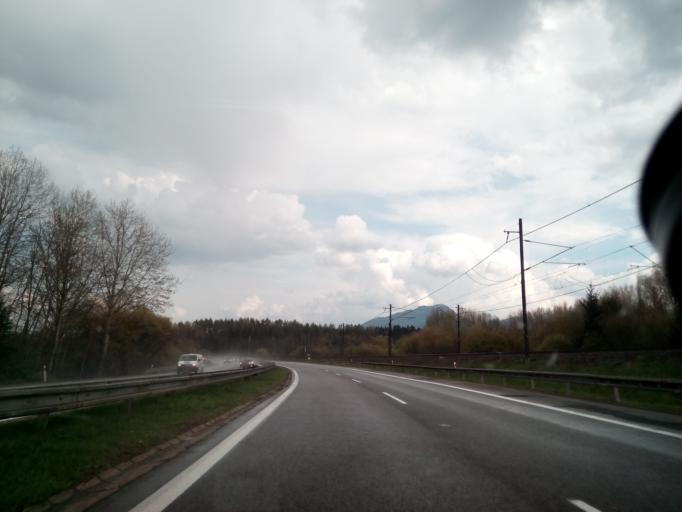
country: SK
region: Zilinsky
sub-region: Okres Liptovsky Mikulas
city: Liptovsky Mikulas
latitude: 49.0883
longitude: 19.5343
